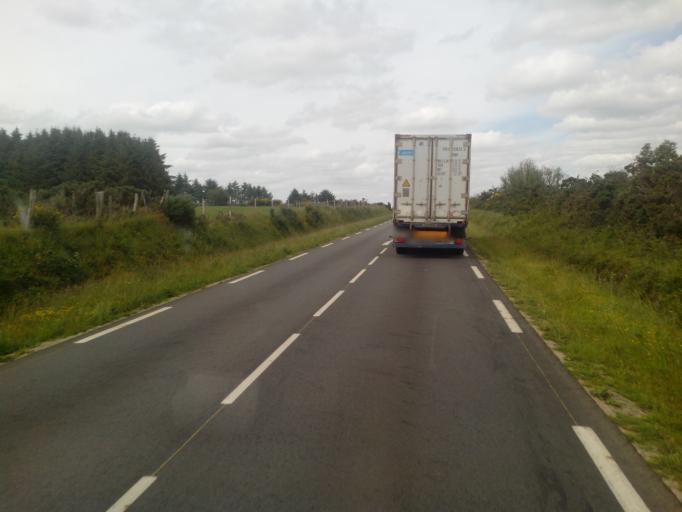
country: FR
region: Brittany
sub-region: Departement du Finistere
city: Guerlesquin
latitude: 48.5484
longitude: -3.5992
